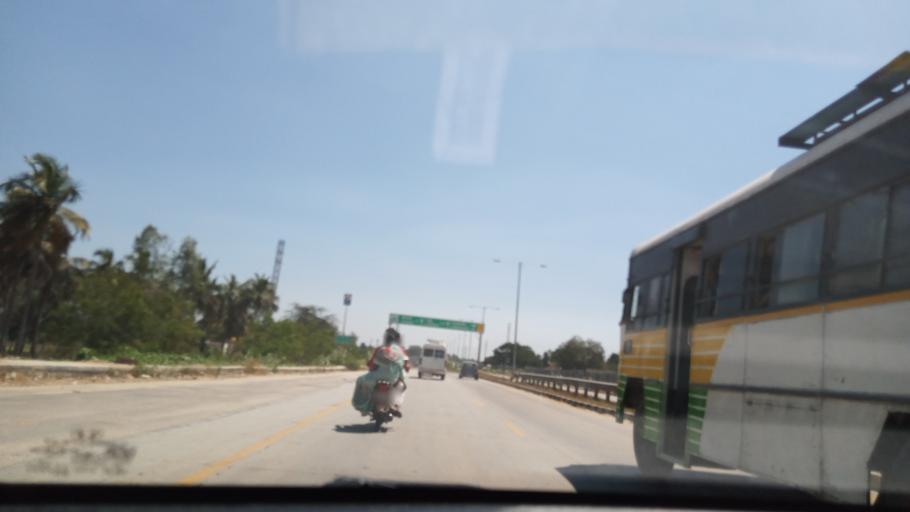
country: IN
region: Andhra Pradesh
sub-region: Chittoor
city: Palmaner
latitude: 13.1995
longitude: 78.7153
